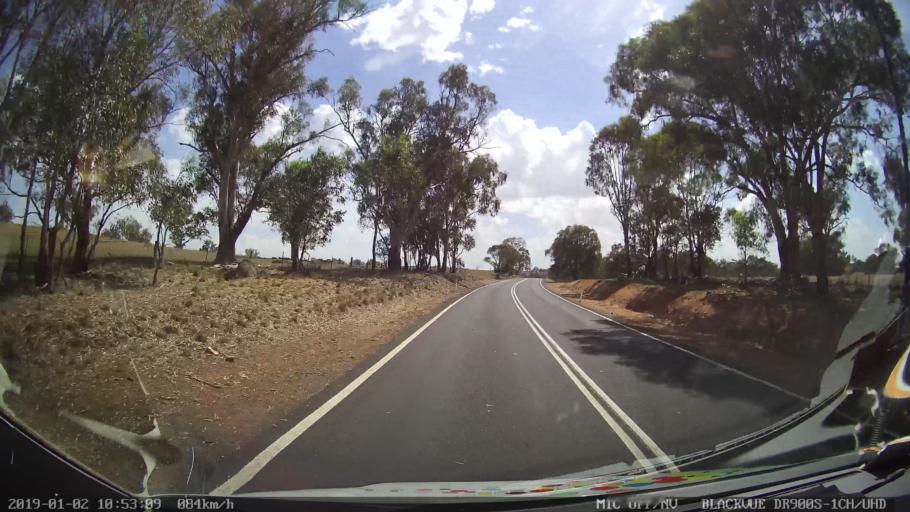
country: AU
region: New South Wales
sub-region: Cootamundra
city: Cootamundra
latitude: -34.6805
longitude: 148.2726
